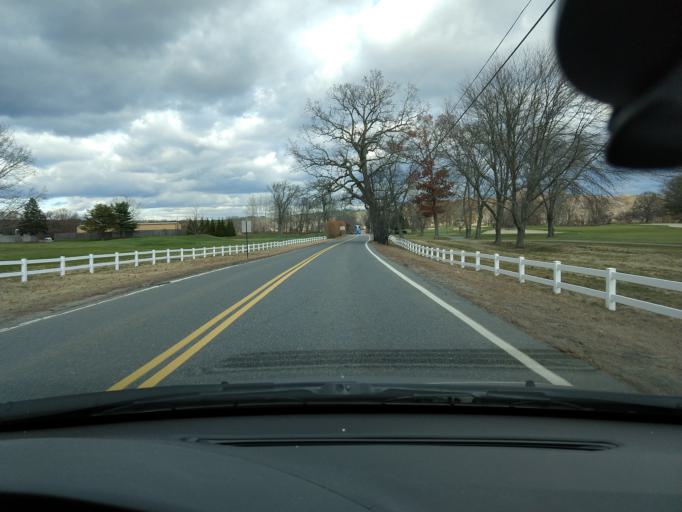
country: US
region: Massachusetts
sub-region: Middlesex County
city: West Concord
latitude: 42.4145
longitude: -71.3753
